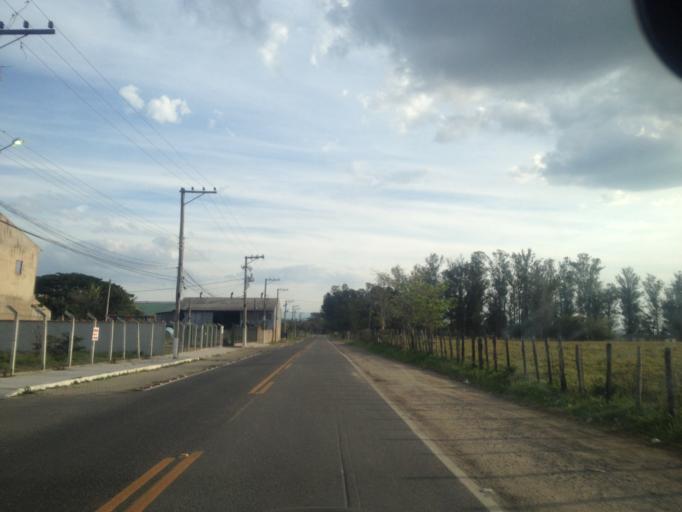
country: BR
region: Rio de Janeiro
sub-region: Quatis
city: Quatis
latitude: -22.4046
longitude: -44.2685
